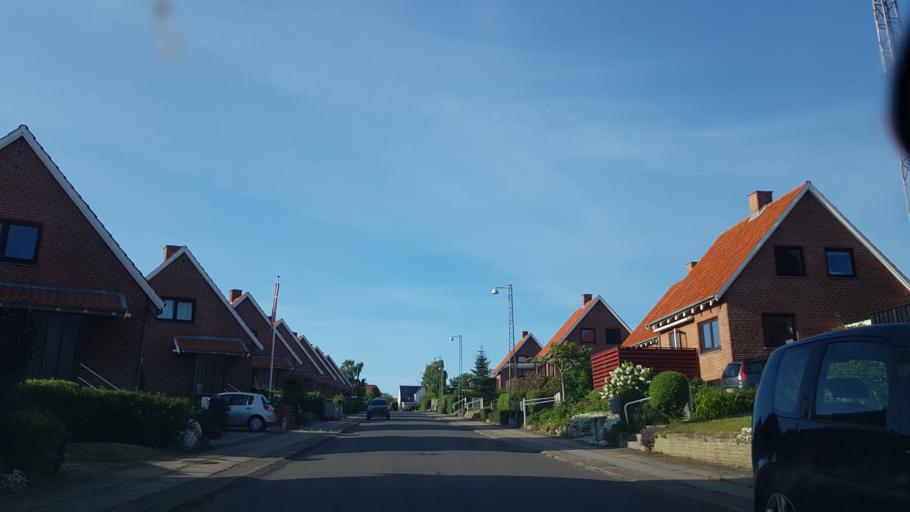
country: DK
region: Zealand
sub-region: Slagelse Kommune
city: Korsor
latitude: 55.3232
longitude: 11.1500
